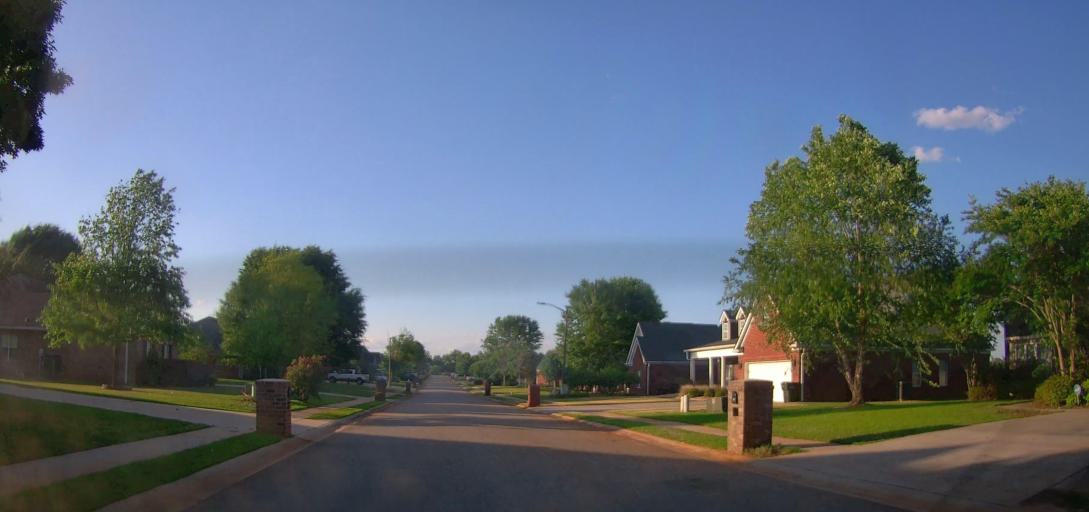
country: US
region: Georgia
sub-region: Houston County
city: Centerville
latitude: 32.6313
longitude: -83.7202
